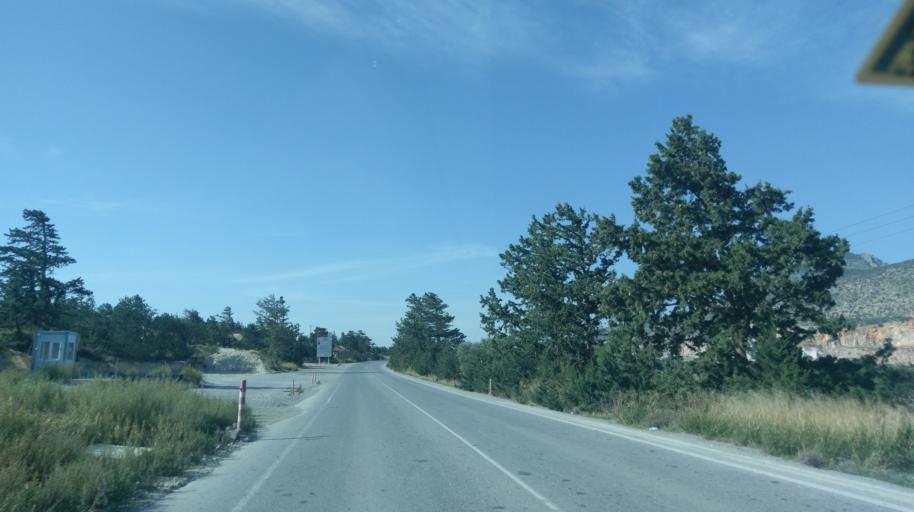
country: CY
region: Lefkosia
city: Nicosia
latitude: 35.2684
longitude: 33.4694
